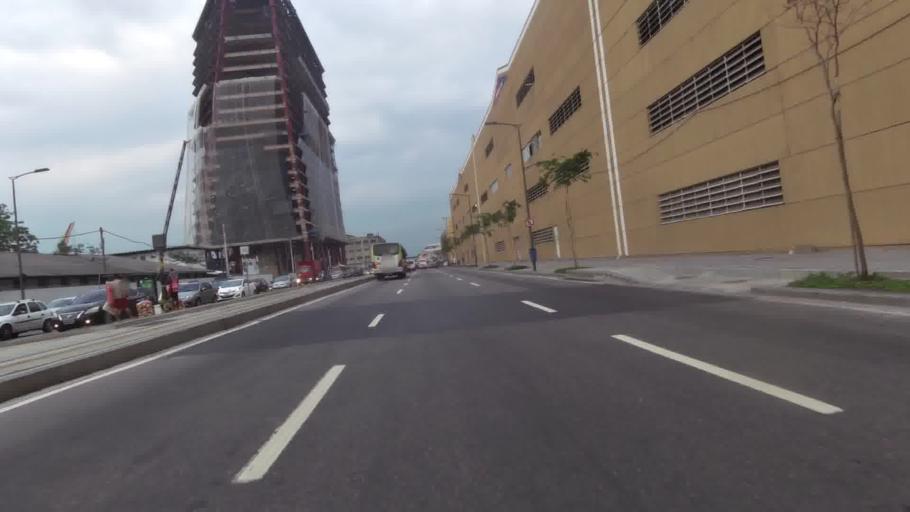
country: BR
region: Rio de Janeiro
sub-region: Rio De Janeiro
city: Rio de Janeiro
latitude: -22.8950
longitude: -43.1986
